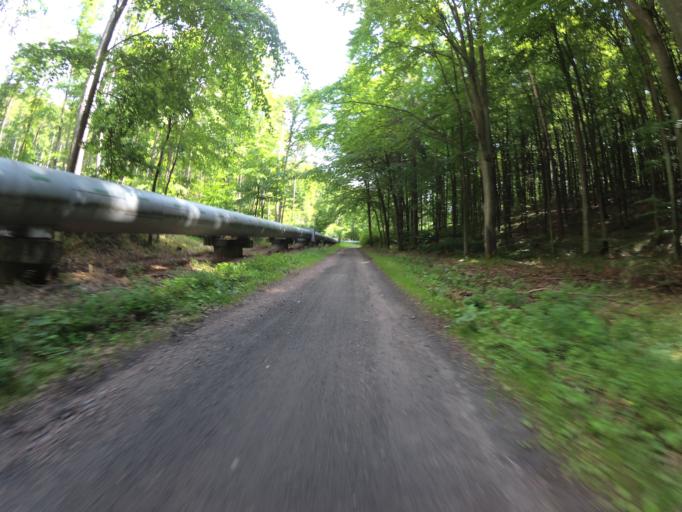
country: PL
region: Pomeranian Voivodeship
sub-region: Gdynia
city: Wielki Kack
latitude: 54.5116
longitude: 18.4834
